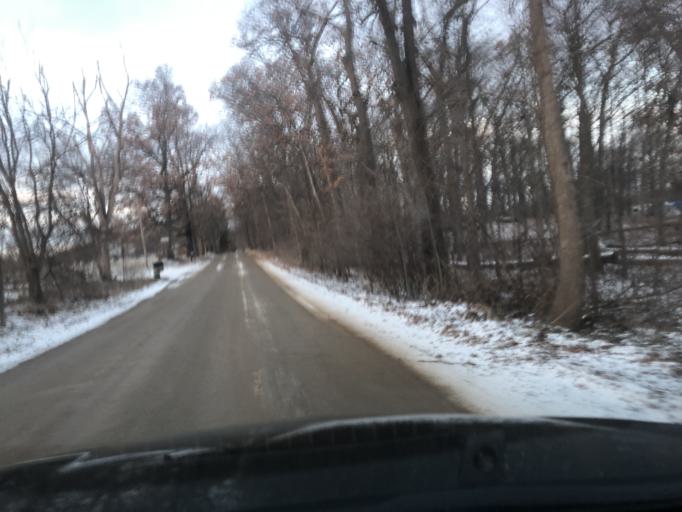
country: US
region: Michigan
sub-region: Oakland County
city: Milford
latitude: 42.5863
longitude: -83.6400
